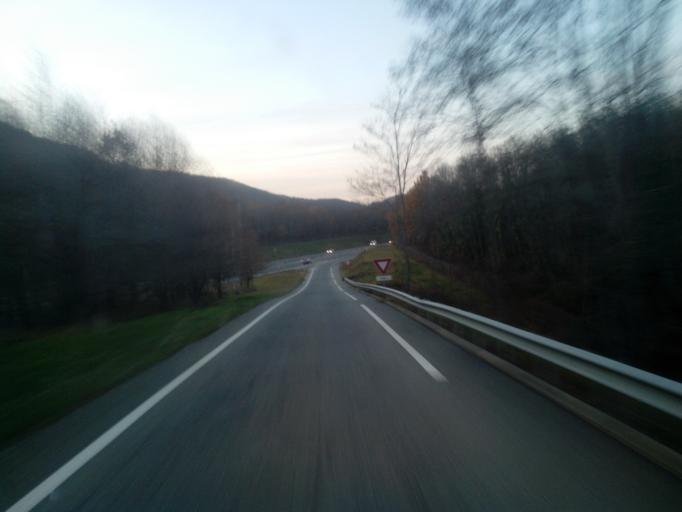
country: FR
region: Midi-Pyrenees
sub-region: Departement de l'Ariege
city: Montgaillard
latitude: 42.9226
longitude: 1.6367
